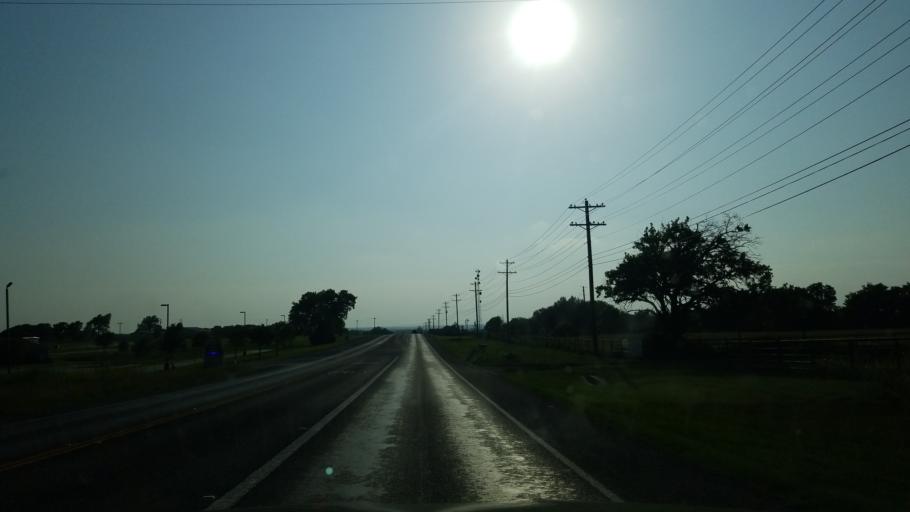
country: US
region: Texas
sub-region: Denton County
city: Aubrey
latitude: 33.3044
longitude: -96.9932
